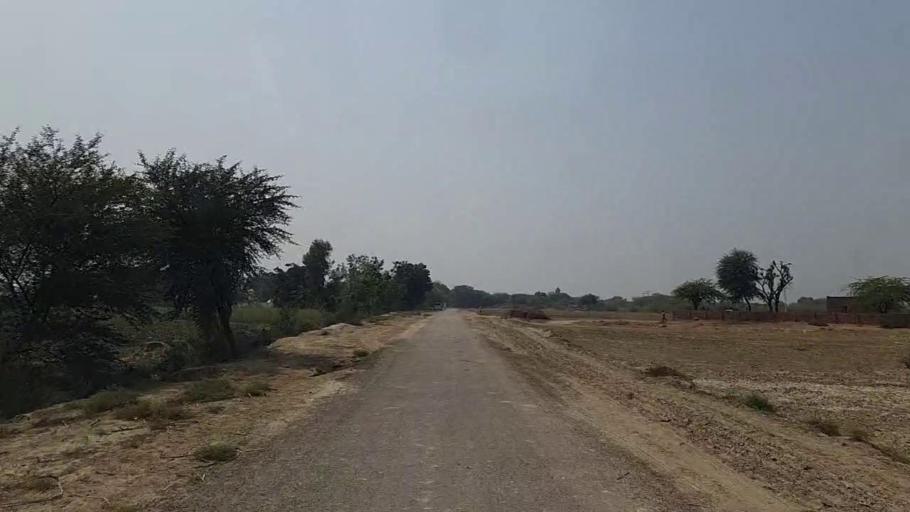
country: PK
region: Sindh
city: Naukot
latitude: 24.8317
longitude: 69.4232
